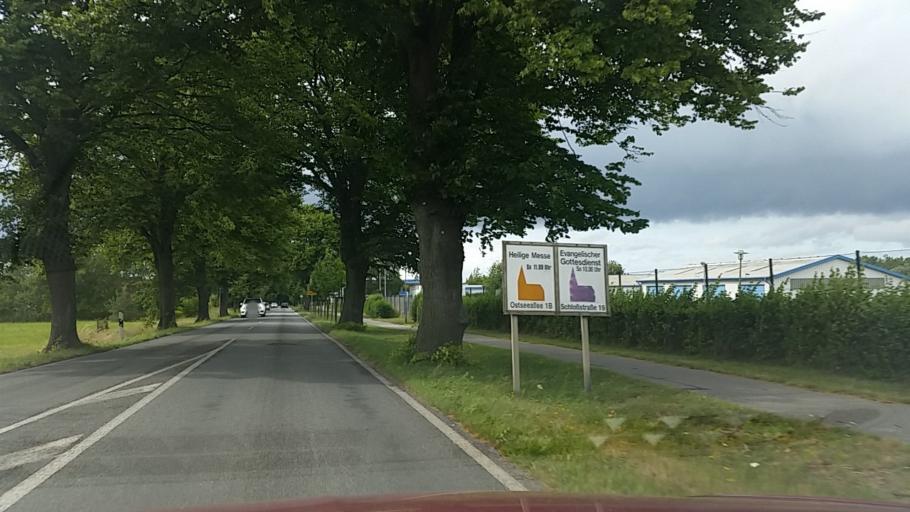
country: DE
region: Mecklenburg-Vorpommern
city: Ostseebad Kuhlungsborn
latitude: 54.1432
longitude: 11.7699
